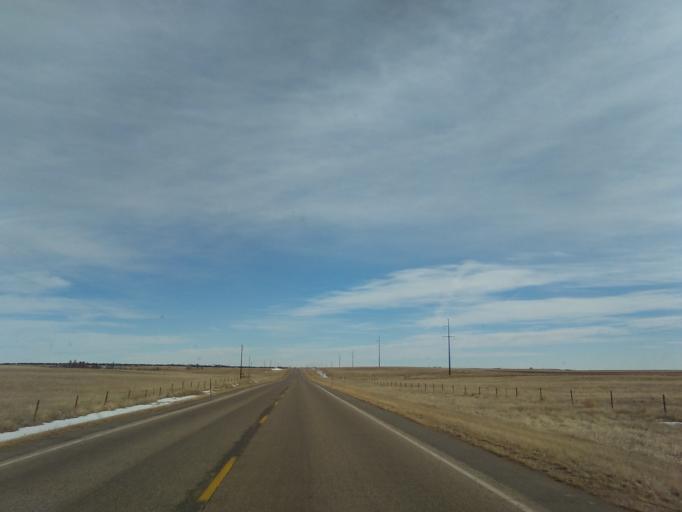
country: US
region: Wyoming
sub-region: Laramie County
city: Ranchettes
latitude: 41.4112
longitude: -104.4342
